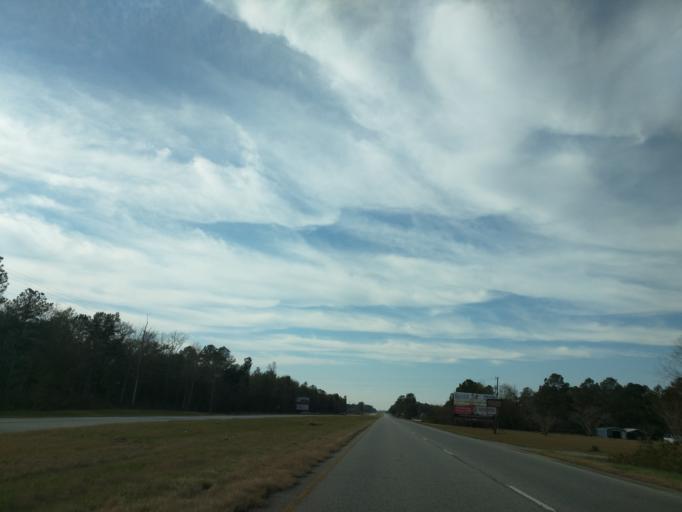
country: US
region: Georgia
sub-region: Decatur County
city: Bainbridge
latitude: 30.8905
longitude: -84.4882
